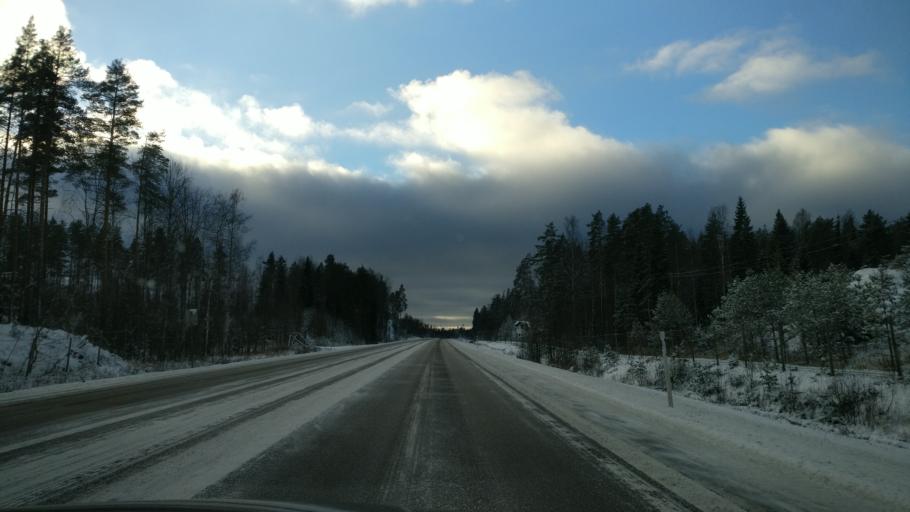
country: FI
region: Paijanne Tavastia
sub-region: Lahti
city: Heinola
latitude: 61.3407
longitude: 26.1893
